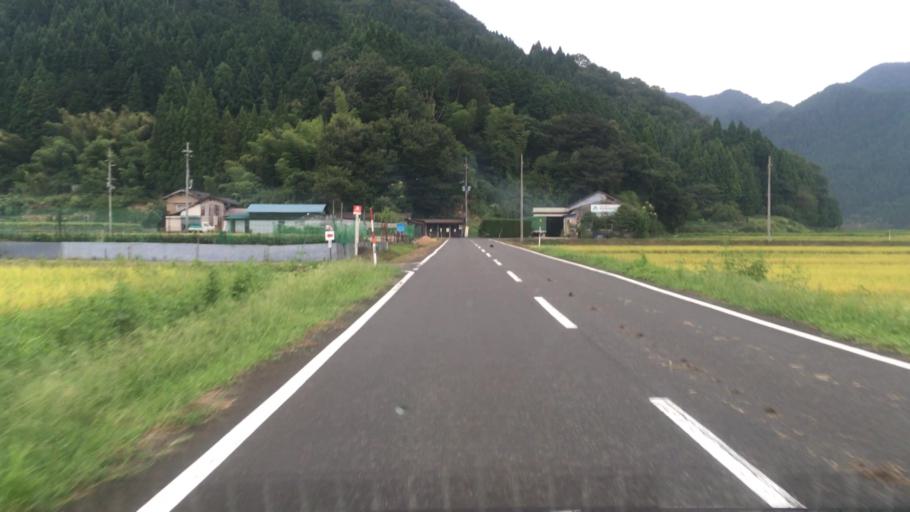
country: JP
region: Hyogo
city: Toyooka
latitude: 35.4529
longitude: 134.7343
